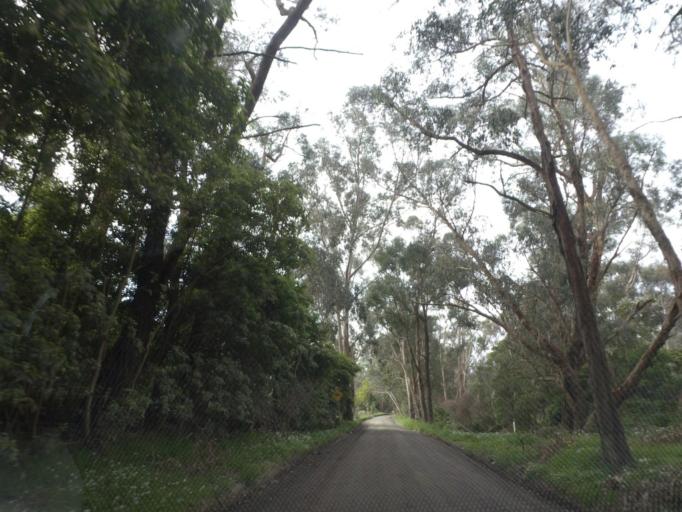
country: AU
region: Victoria
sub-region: Knox
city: The Basin
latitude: -37.8462
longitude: 145.3262
